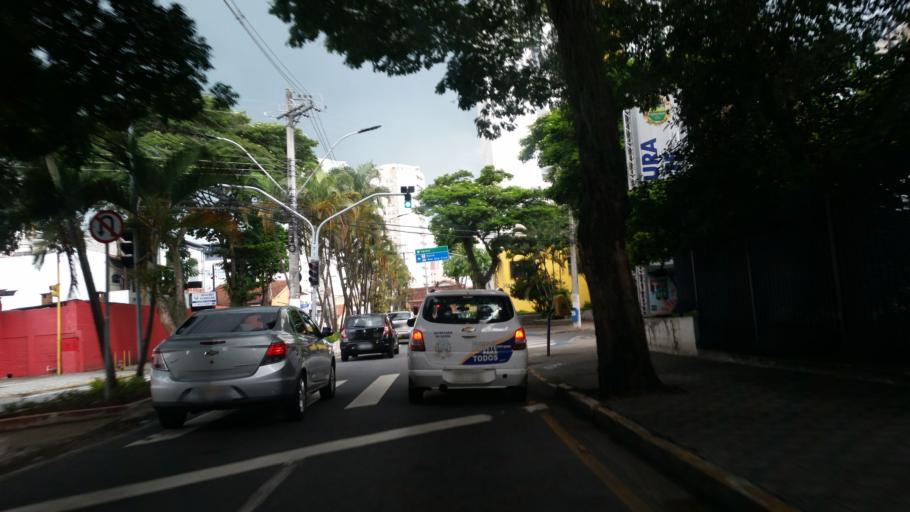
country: BR
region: Sao Paulo
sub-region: Taubate
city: Taubate
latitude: -23.0311
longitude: -45.5653
